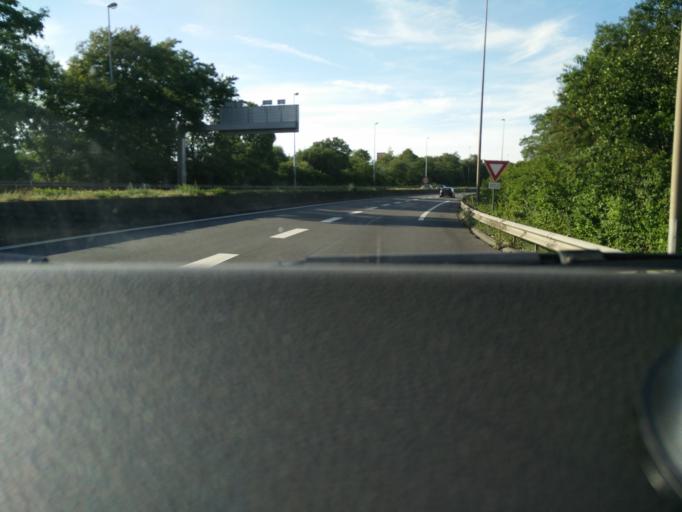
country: FR
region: Nord-Pas-de-Calais
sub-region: Departement du Nord
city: Douchy-les-Mines
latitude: 50.3045
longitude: 3.3721
